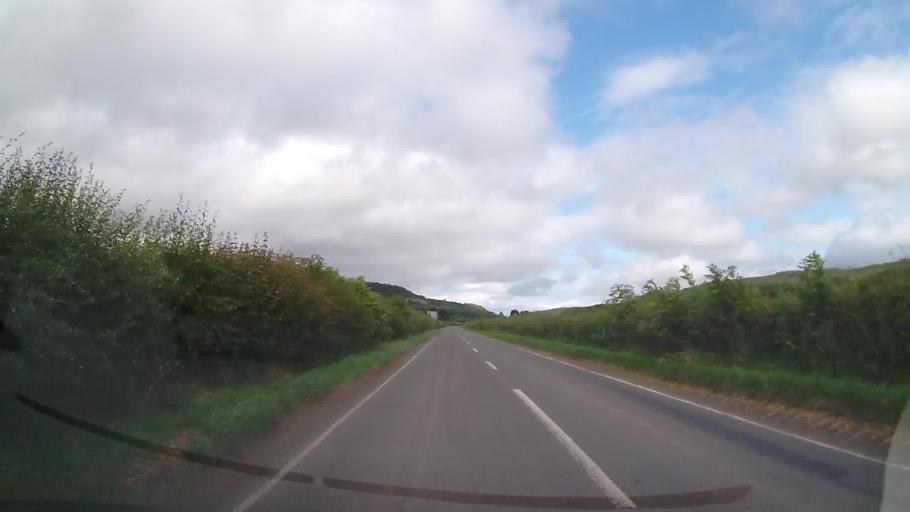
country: GB
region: England
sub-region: Shropshire
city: Pant
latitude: 52.8002
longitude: -3.1146
